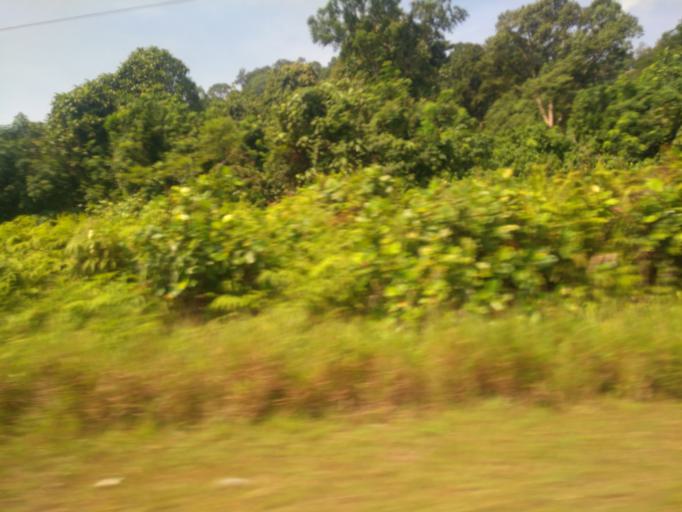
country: MY
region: Sarawak
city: Kuching
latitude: 1.6482
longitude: 110.1852
